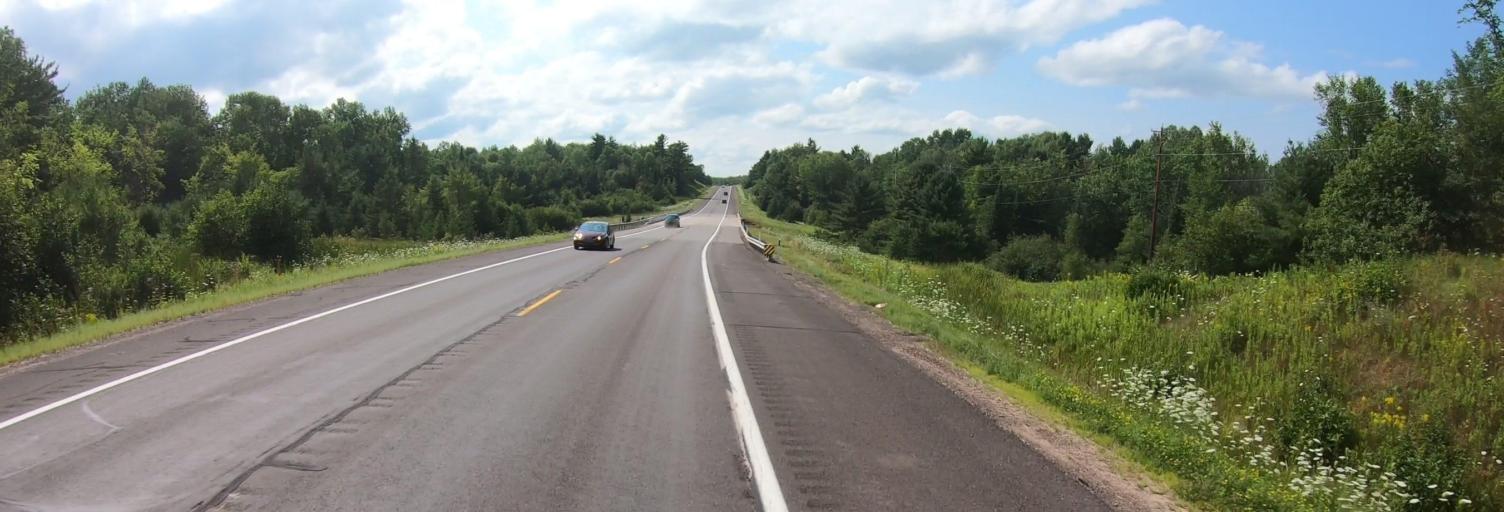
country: US
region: Michigan
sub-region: Ontonagon County
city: Ontonagon
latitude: 46.5329
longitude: -89.2034
